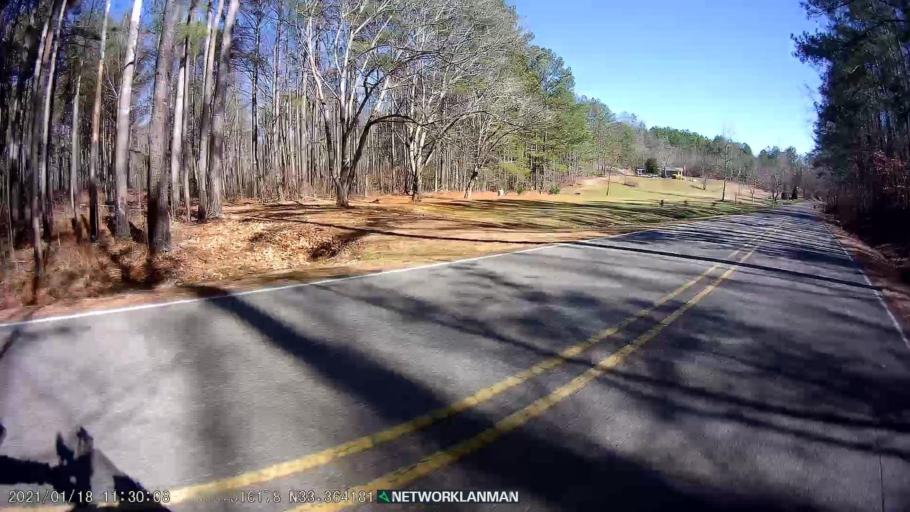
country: US
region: Alabama
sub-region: Clay County
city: Ashland
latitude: 33.3642
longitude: -85.9163
